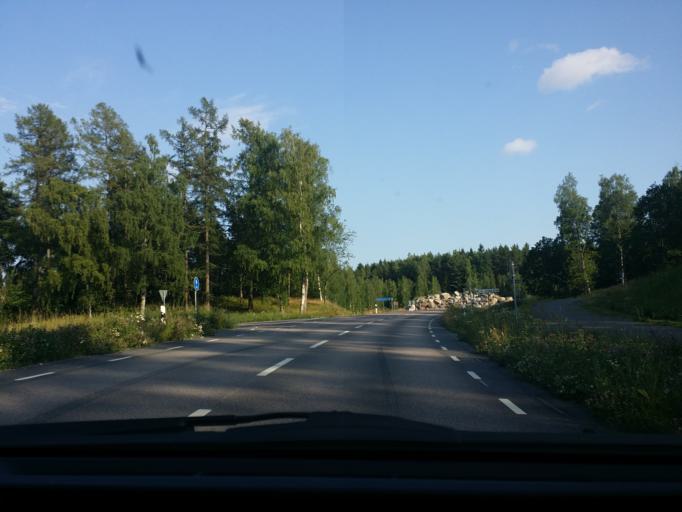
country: SE
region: Vaestmanland
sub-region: Vasteras
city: Tillberga
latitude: 59.5768
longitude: 16.6743
